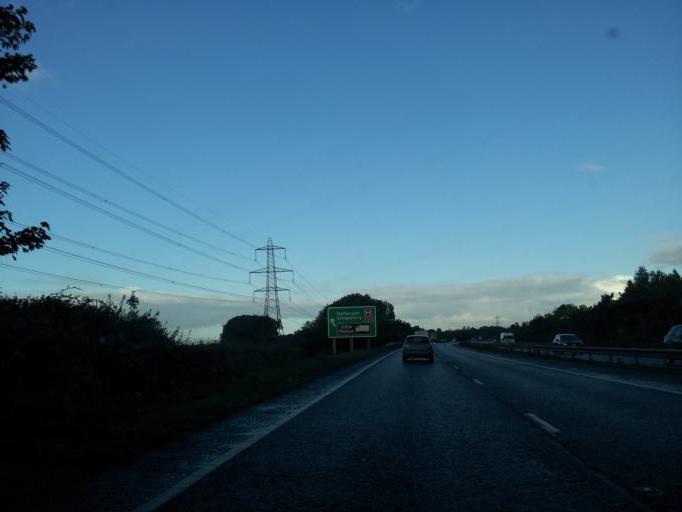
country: GB
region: England
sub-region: Norfolk
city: Cringleford
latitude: 52.5959
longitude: 1.2368
